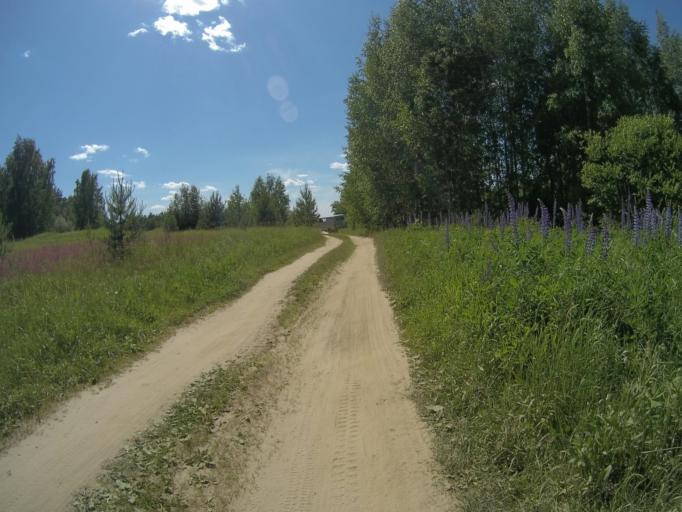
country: RU
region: Vladimir
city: Golovino
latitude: 56.0034
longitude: 40.4415
